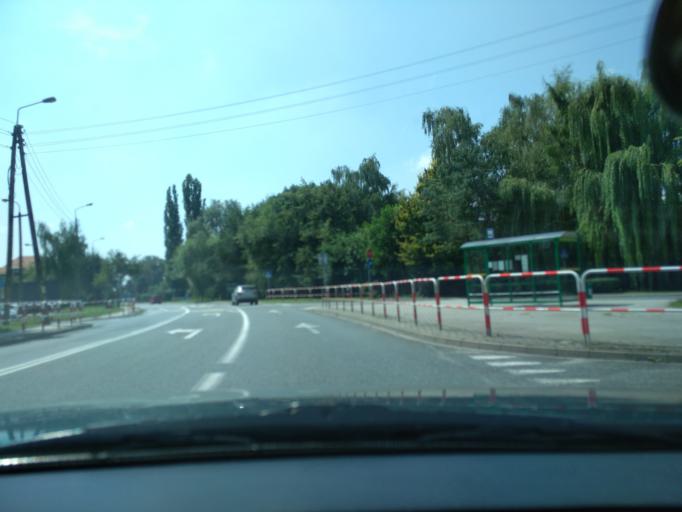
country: PL
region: Silesian Voivodeship
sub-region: Powiat raciborski
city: Raciborz
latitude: 50.0874
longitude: 18.1964
